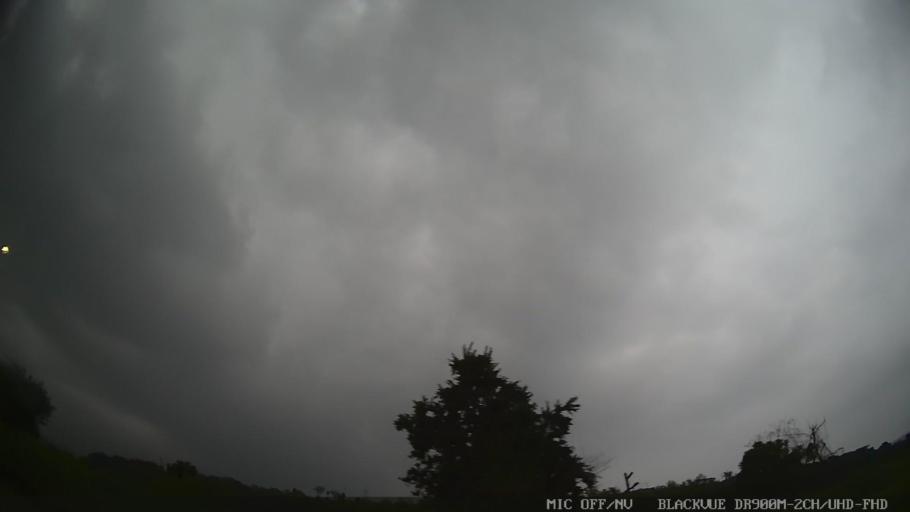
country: BR
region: Sao Paulo
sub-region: Jarinu
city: Jarinu
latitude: -22.9590
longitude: -46.6989
